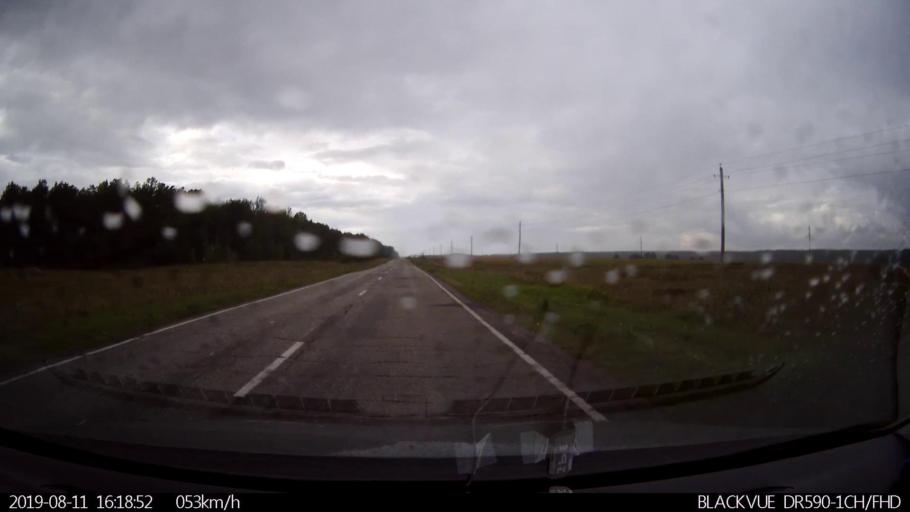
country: RU
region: Ulyanovsk
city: Mayna
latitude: 54.0592
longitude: 47.6094
